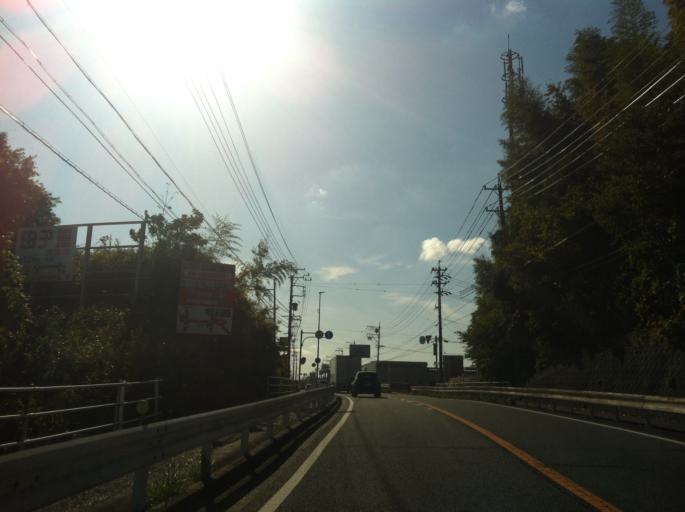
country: JP
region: Shizuoka
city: Fujieda
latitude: 34.8837
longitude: 138.2744
